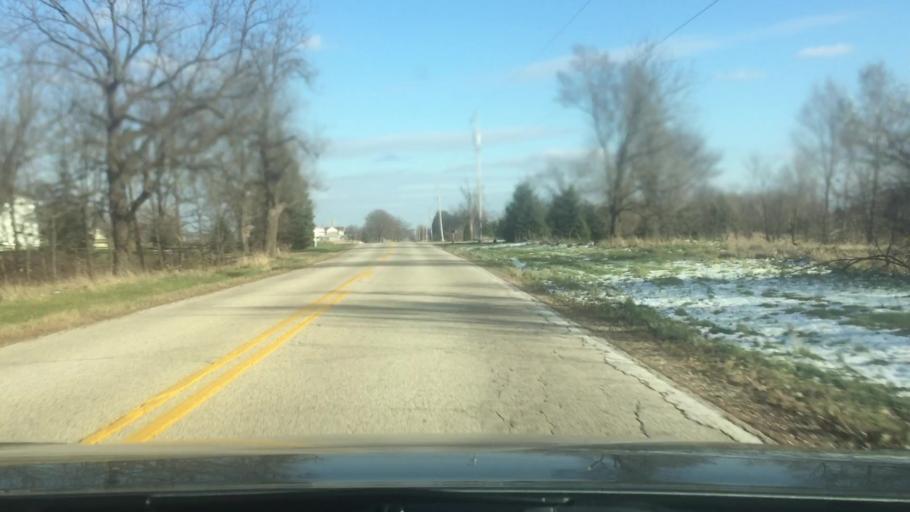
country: US
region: Wisconsin
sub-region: Jefferson County
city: Palmyra
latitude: 42.9173
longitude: -88.5404
